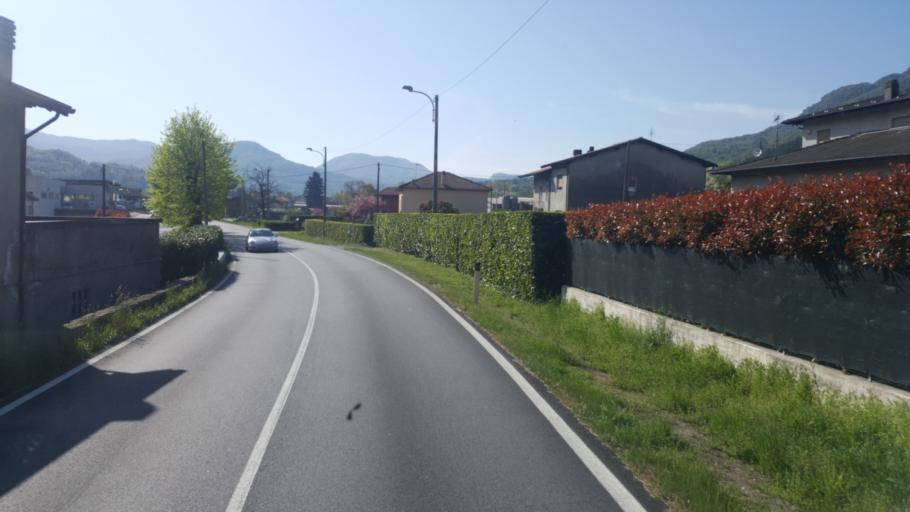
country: IT
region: Lombardy
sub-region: Provincia di Varese
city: Mesenzana
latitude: 45.9611
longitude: 8.7559
